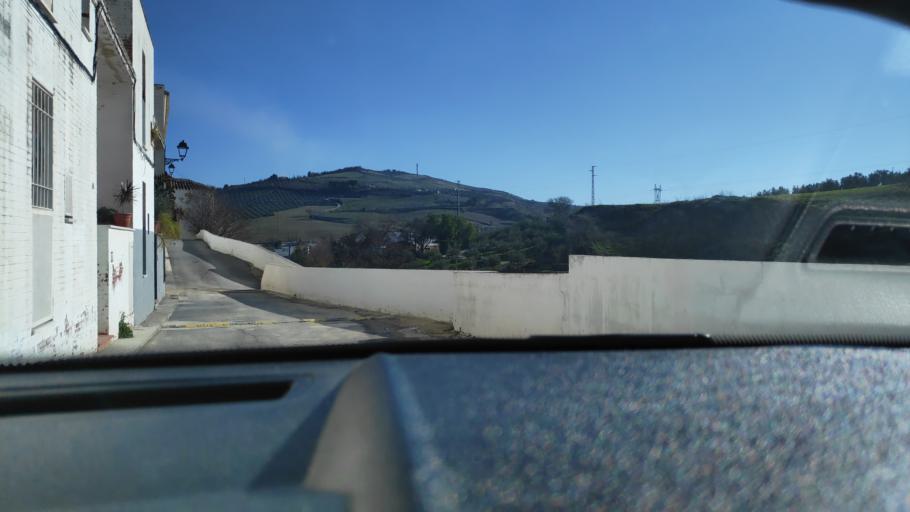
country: ES
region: Andalusia
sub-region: Province of Cordoba
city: Baena
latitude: 37.6115
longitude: -4.3266
